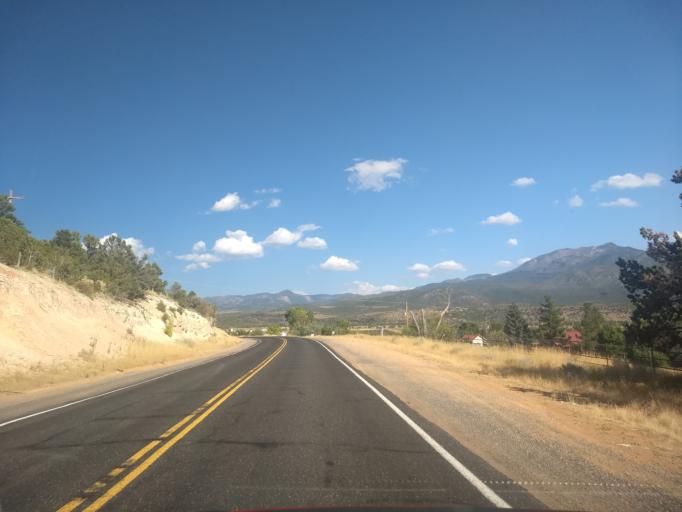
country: US
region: Utah
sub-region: Washington County
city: Enterprise
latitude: 37.4169
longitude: -113.6260
